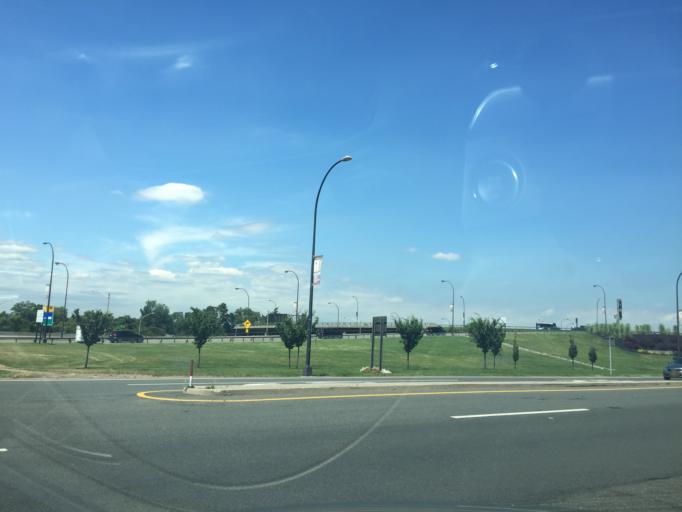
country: US
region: New Jersey
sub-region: Union County
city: Elizabeth
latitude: 40.6920
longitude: -74.1881
